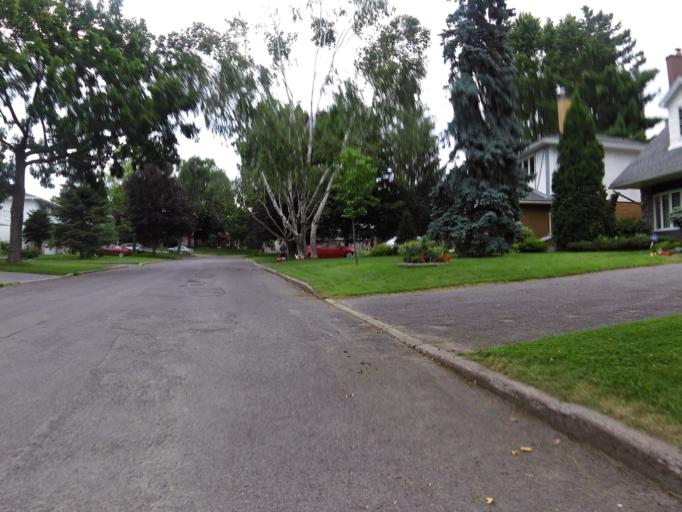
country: CA
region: Ontario
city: Bells Corners
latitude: 45.3662
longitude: -75.7769
